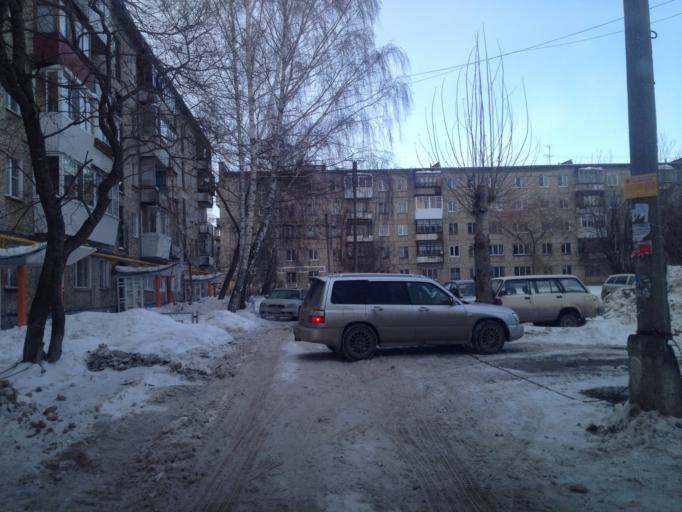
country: RU
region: Sverdlovsk
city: Yekaterinburg
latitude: 56.9064
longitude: 60.6016
